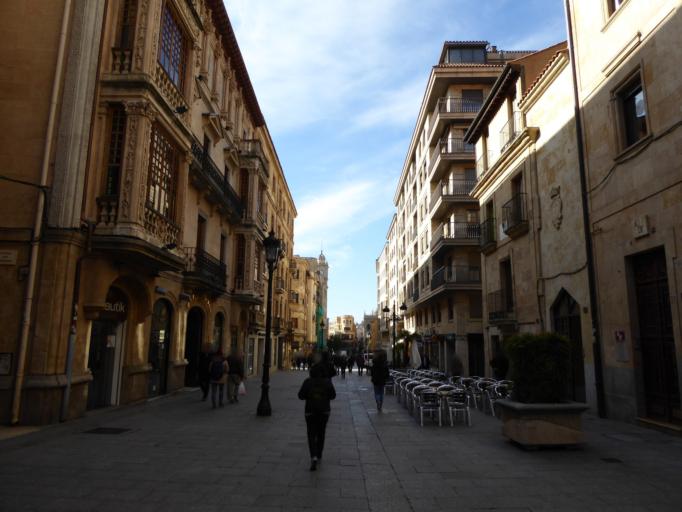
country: ES
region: Castille and Leon
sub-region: Provincia de Salamanca
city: Salamanca
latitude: 40.9686
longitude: -5.6637
